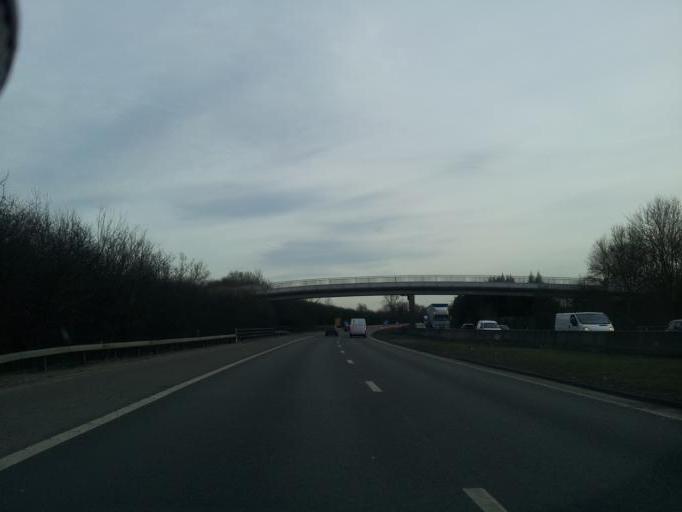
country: GB
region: England
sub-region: Hertfordshire
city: Hatfield
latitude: 51.7253
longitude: -0.2246
